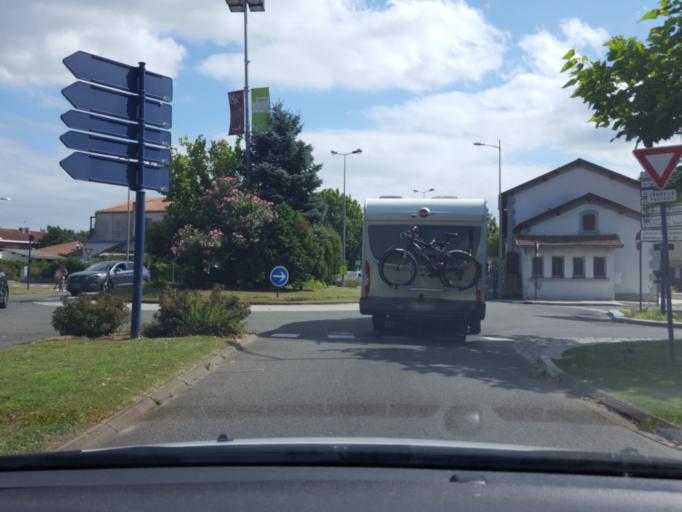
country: FR
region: Aquitaine
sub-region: Departement des Landes
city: Capbreton
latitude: 43.6412
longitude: -1.4257
